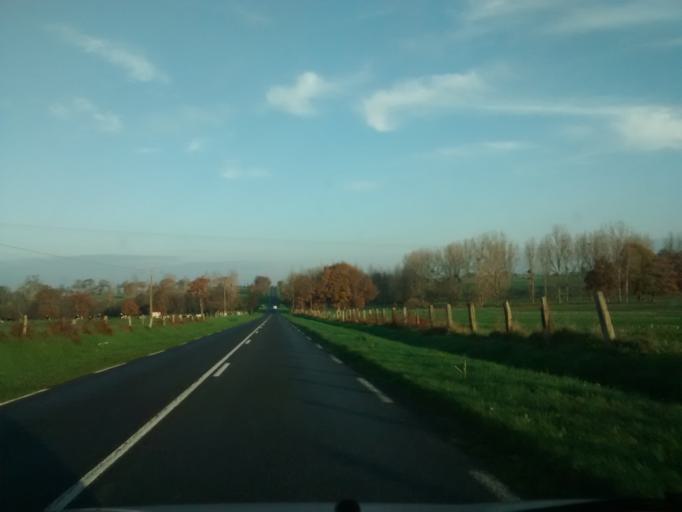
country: FR
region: Brittany
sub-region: Departement d'Ille-et-Vilaine
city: Antrain
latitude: 48.5113
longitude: -1.4777
